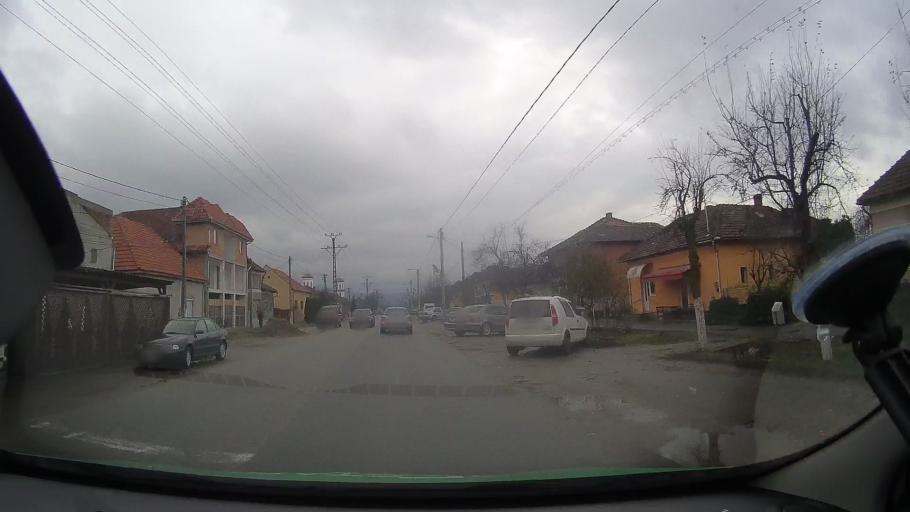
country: RO
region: Arad
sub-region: Comuna Sebis
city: Sebis
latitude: 46.3696
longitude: 22.1310
